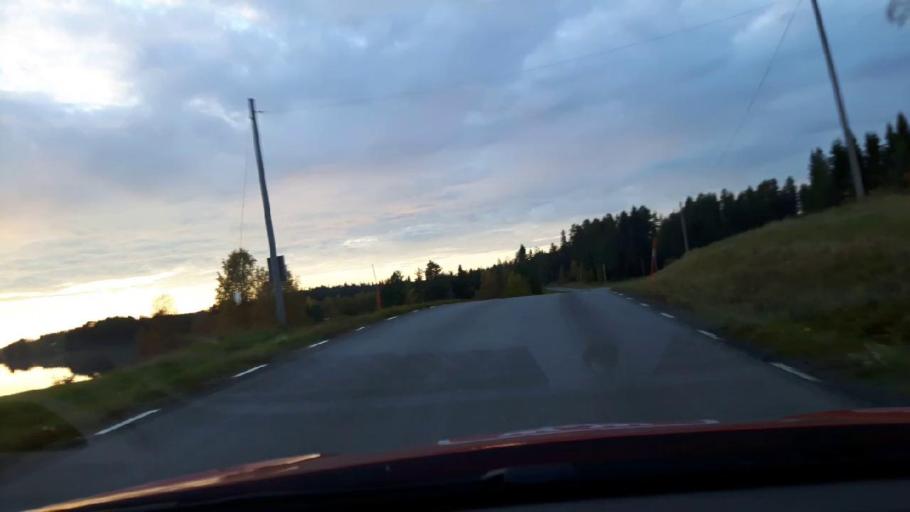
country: SE
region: Jaemtland
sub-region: OEstersunds Kommun
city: Lit
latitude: 63.3196
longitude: 14.9495
